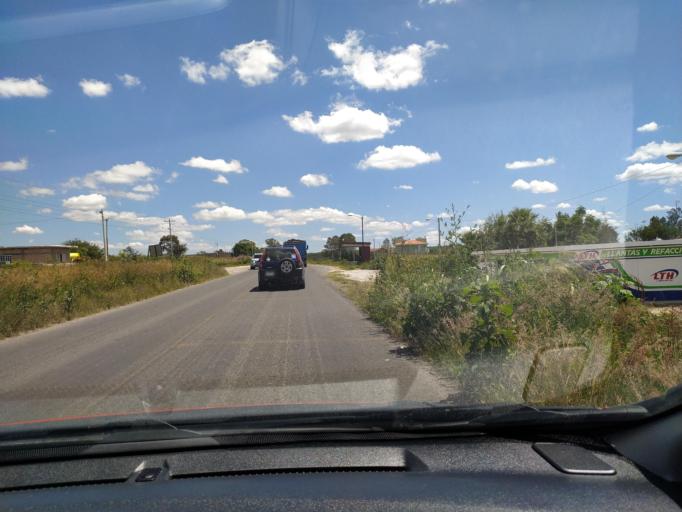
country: MX
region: Jalisco
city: San Diego de Alejandria
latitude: 21.0068
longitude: -102.0411
